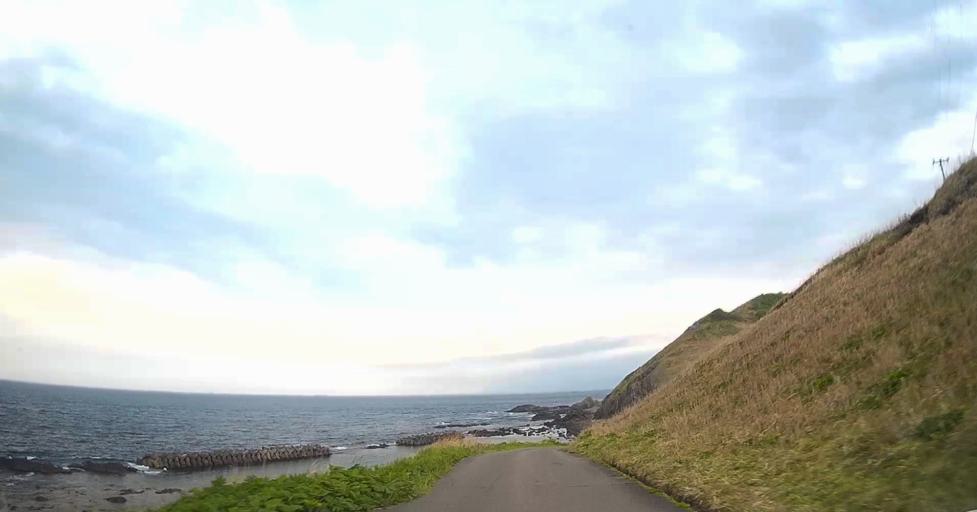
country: JP
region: Aomori
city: Shimokizukuri
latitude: 41.2506
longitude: 140.3438
